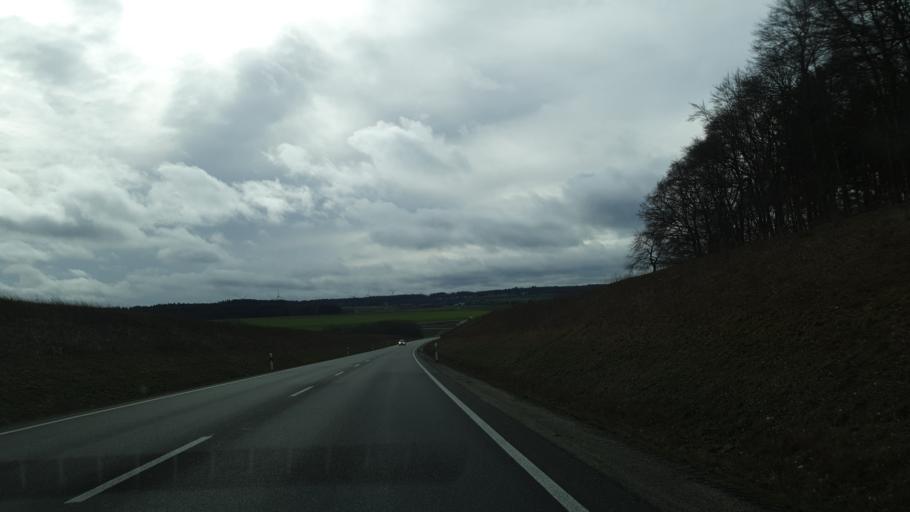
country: DE
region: Rheinland-Pfalz
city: Braunshorn
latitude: 50.0905
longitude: 7.5051
